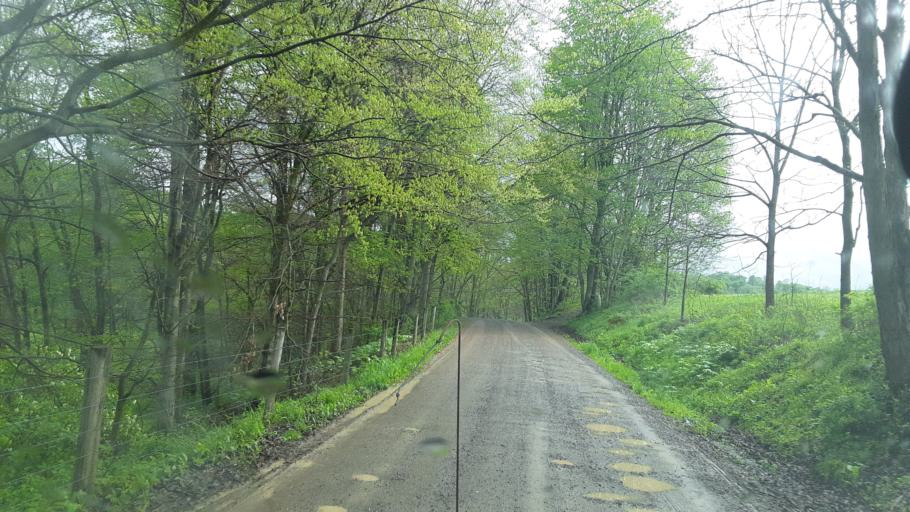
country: US
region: Ohio
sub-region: Holmes County
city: Millersburg
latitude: 40.4977
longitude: -81.8342
